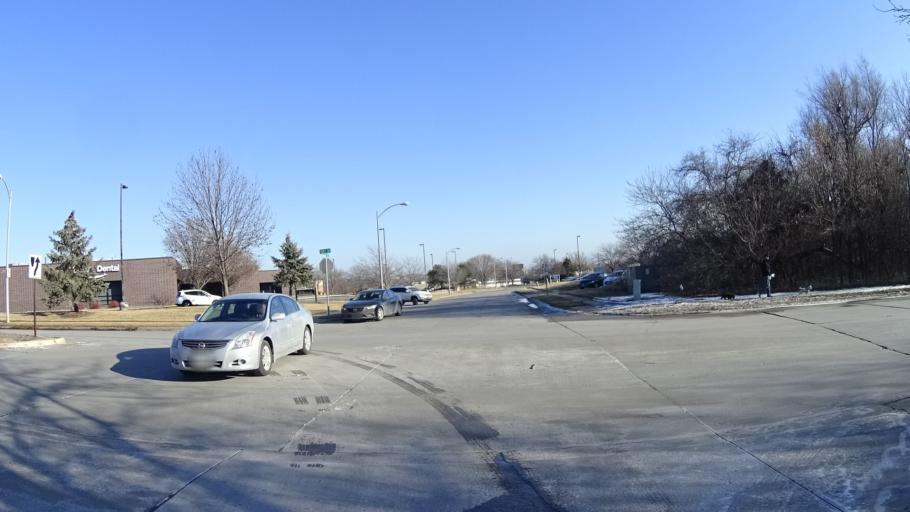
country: US
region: Nebraska
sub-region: Douglas County
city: Bennington
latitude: 41.2914
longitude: -96.1058
